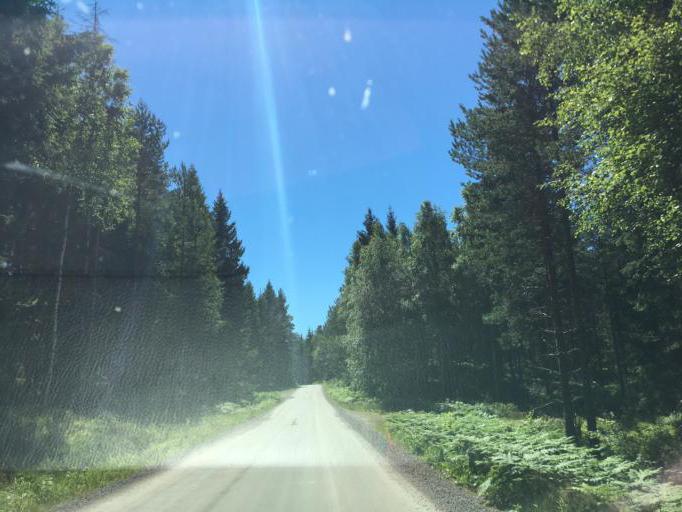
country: SE
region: Vaestra Goetaland
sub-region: Karlsborgs Kommun
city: Karlsborg
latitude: 58.7356
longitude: 14.5879
